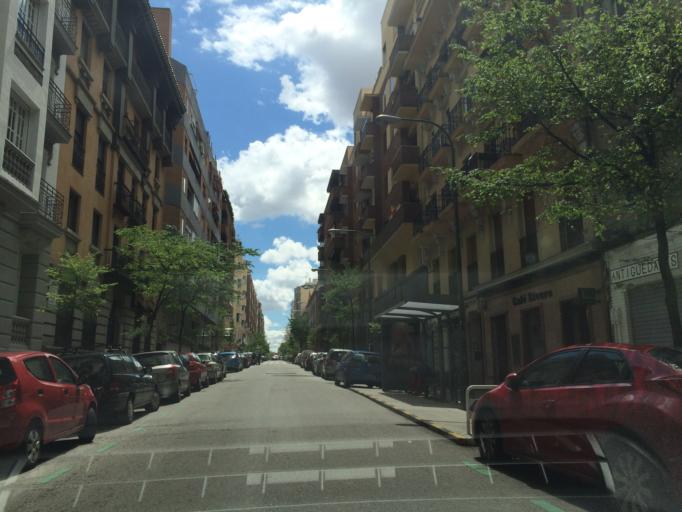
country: ES
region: Madrid
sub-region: Provincia de Madrid
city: Chamberi
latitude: 40.4415
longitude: -3.6960
